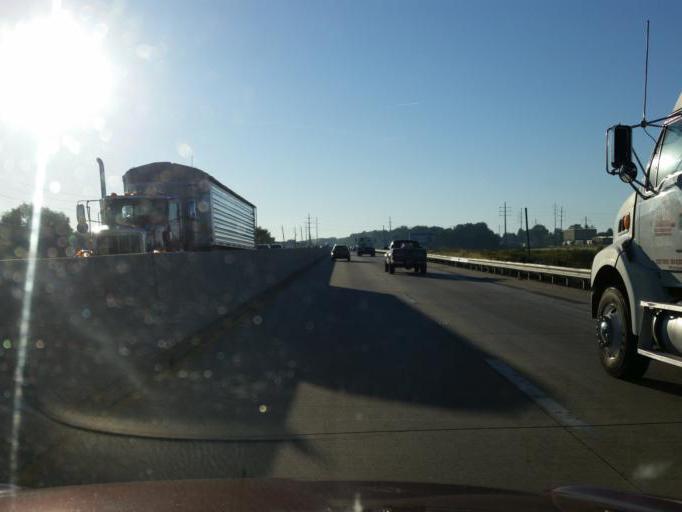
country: US
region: Pennsylvania
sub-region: Lancaster County
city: Salunga
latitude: 40.1027
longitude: -76.4214
